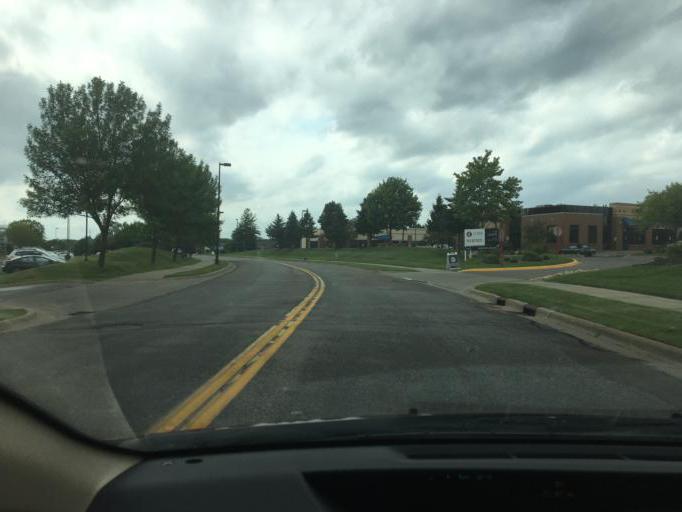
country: US
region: Minnesota
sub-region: Carver County
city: Chanhassen
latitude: 44.8606
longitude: -93.5166
